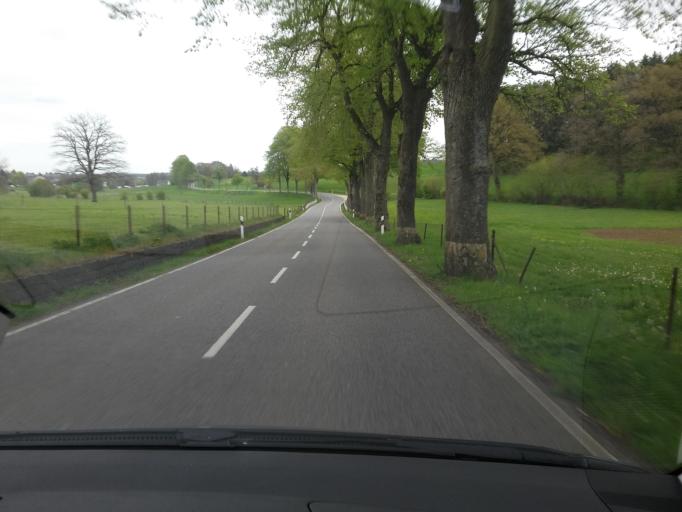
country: LU
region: Luxembourg
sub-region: Canton de Capellen
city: Garnich
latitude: 49.6081
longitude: 5.9392
